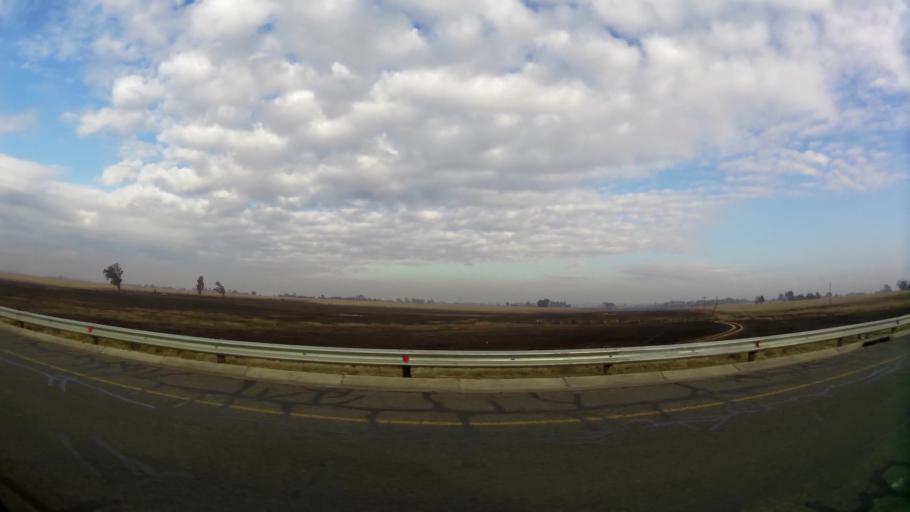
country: ZA
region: Gauteng
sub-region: Sedibeng District Municipality
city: Vanderbijlpark
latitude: -26.6517
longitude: 27.7808
